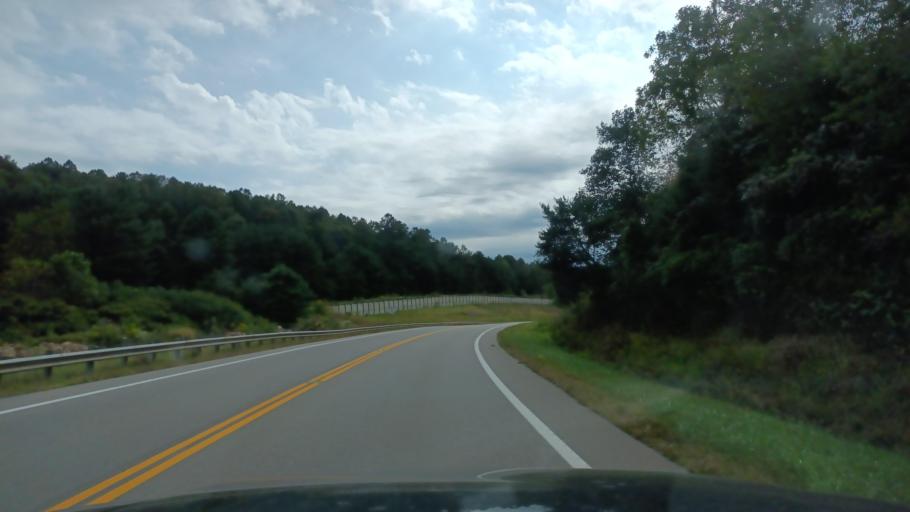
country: US
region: Ohio
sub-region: Jackson County
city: Wellston
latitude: 39.2621
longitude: -82.6815
